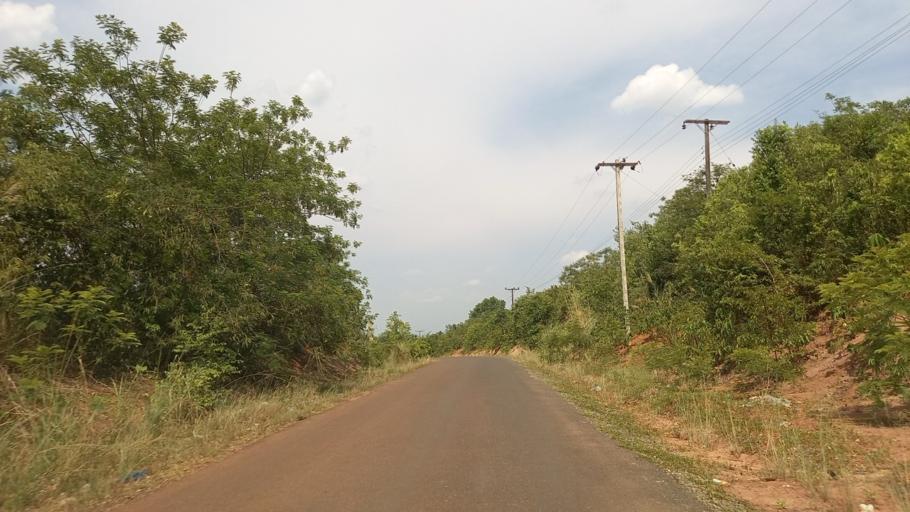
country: LA
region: Bolikhamxai
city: Muang Pakxan
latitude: 18.4287
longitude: 103.7314
